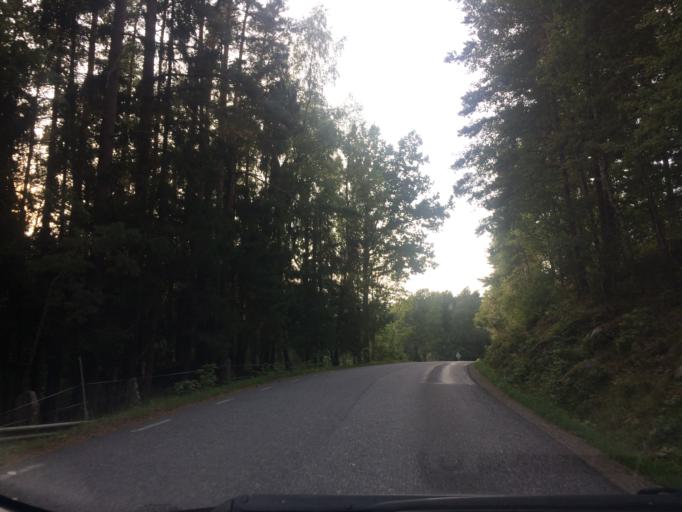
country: SE
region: Vaestra Goetaland
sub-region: Alingsas Kommun
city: Alingsas
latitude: 58.0131
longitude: 12.5483
